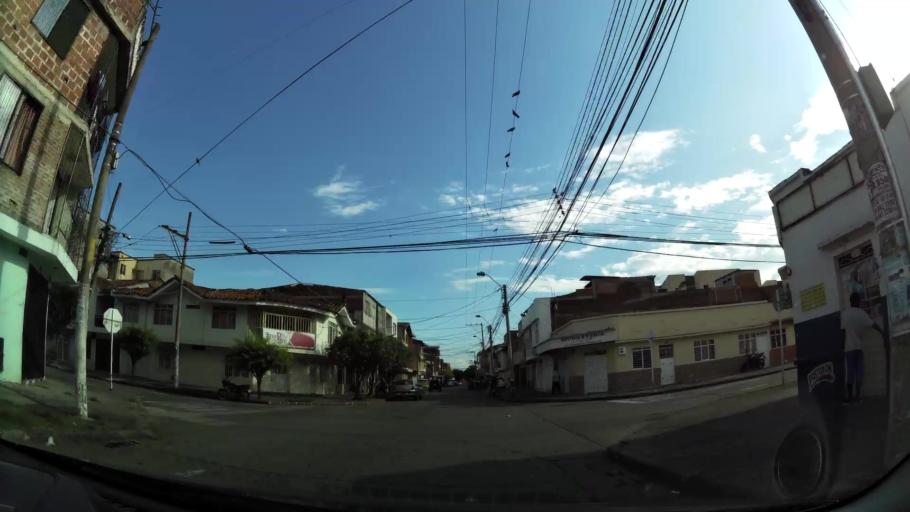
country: CO
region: Valle del Cauca
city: Cali
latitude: 3.4275
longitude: -76.5270
